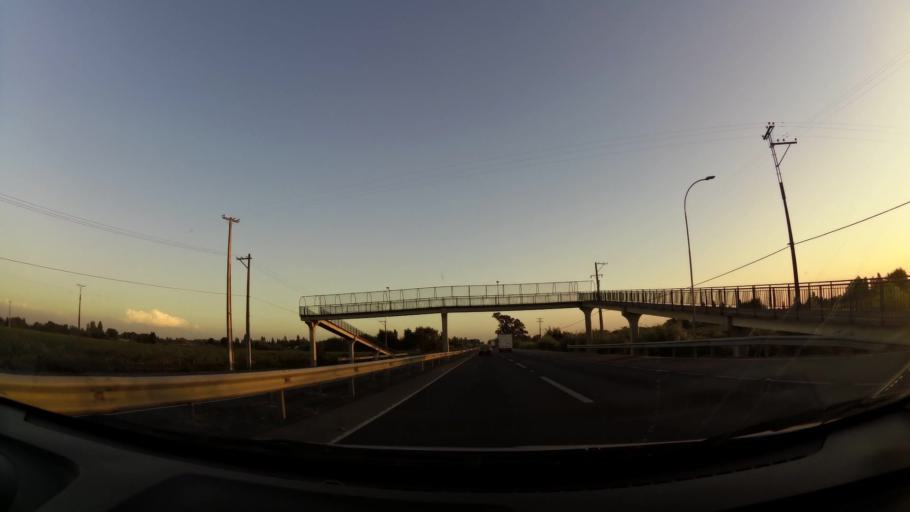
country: CL
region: Maule
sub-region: Provincia de Linares
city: San Javier
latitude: -35.6688
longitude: -71.6915
